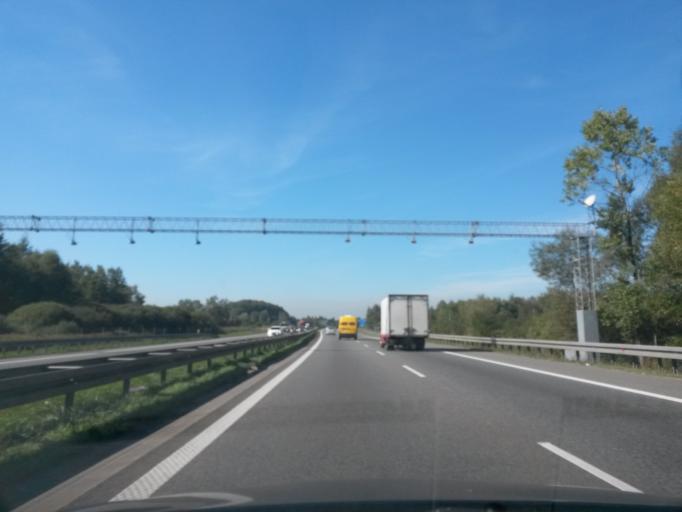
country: PL
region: Lesser Poland Voivodeship
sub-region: Powiat krakowski
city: Skawina
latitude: 50.0169
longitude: 19.8395
